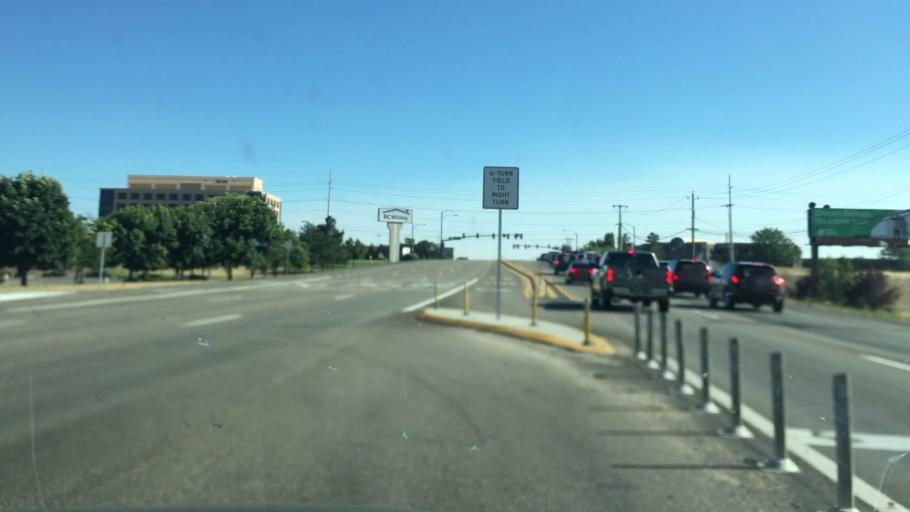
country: US
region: Idaho
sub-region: Ada County
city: Meridian
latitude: 43.6073
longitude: -116.3548
